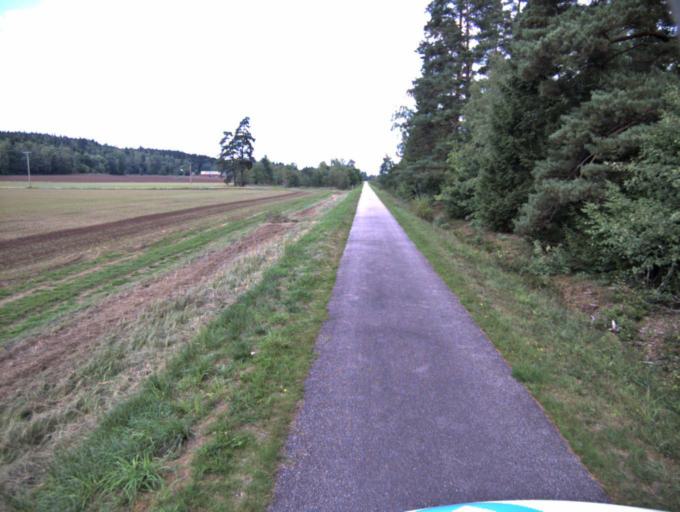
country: SE
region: Vaestra Goetaland
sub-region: Ulricehamns Kommun
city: Ulricehamn
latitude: 57.8330
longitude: 13.4193
